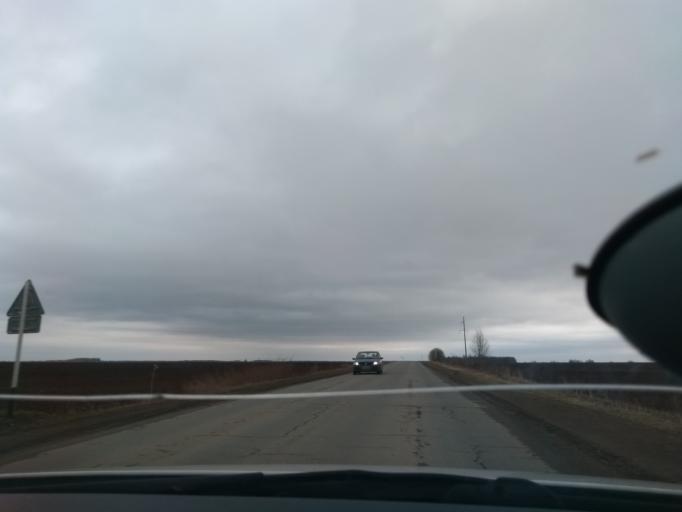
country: RU
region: Perm
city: Kungur
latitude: 57.3752
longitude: 56.8413
